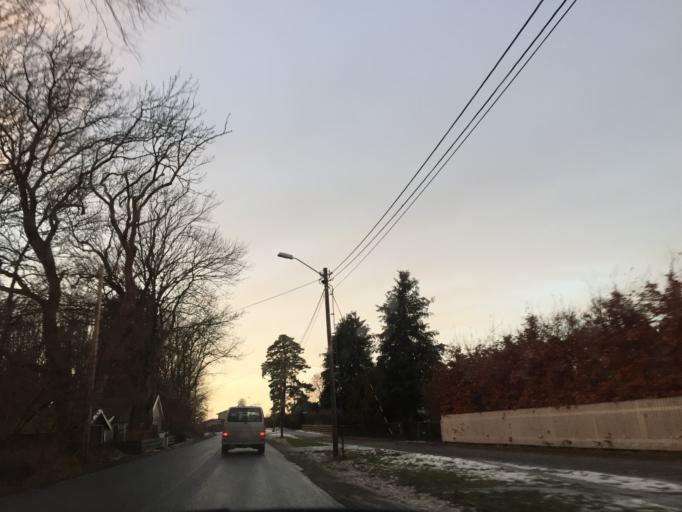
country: NO
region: Ostfold
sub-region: Moss
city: Moss
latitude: 59.4362
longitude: 10.6175
